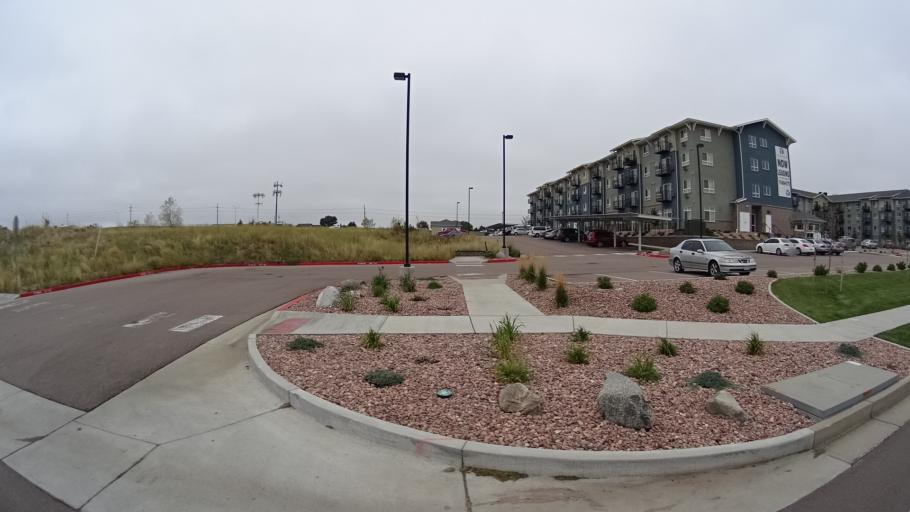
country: US
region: Colorado
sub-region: El Paso County
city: Cimarron Hills
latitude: 38.9180
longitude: -104.7174
